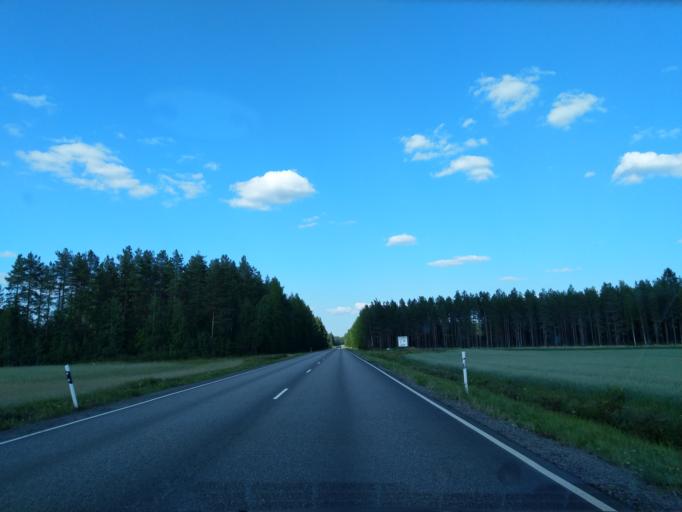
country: FI
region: Pirkanmaa
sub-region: Luoteis-Pirkanmaa
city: Kihnioe
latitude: 62.2103
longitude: 23.2422
